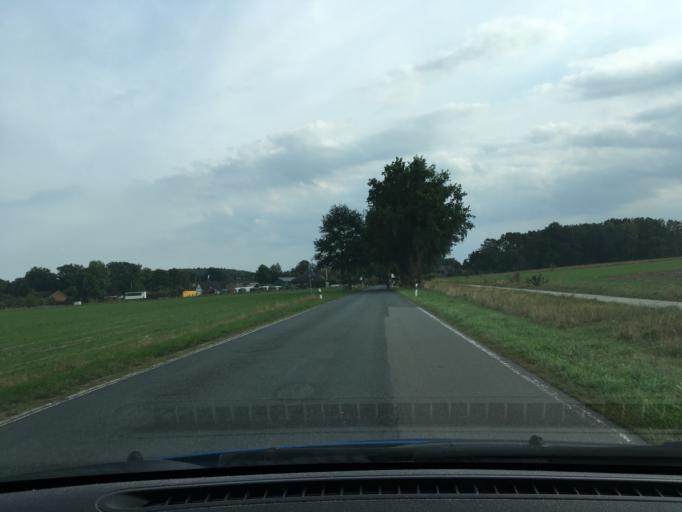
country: DE
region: Lower Saxony
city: Asendorf
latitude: 53.2721
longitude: 9.9744
